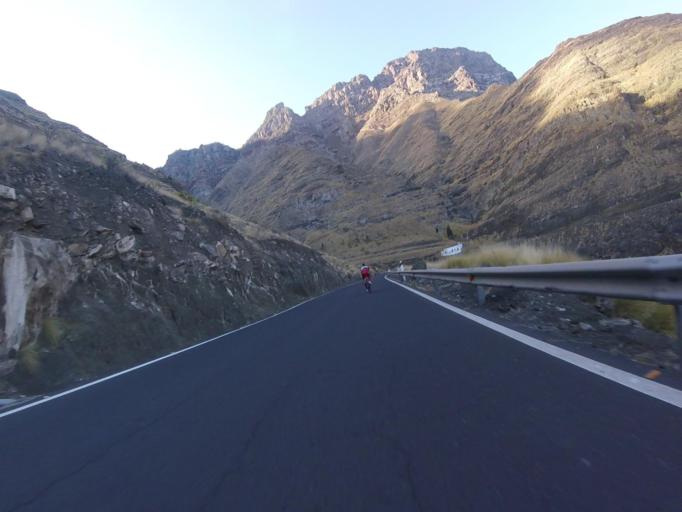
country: ES
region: Canary Islands
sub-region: Provincia de Las Palmas
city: Agaete
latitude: 28.0718
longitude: -15.7109
